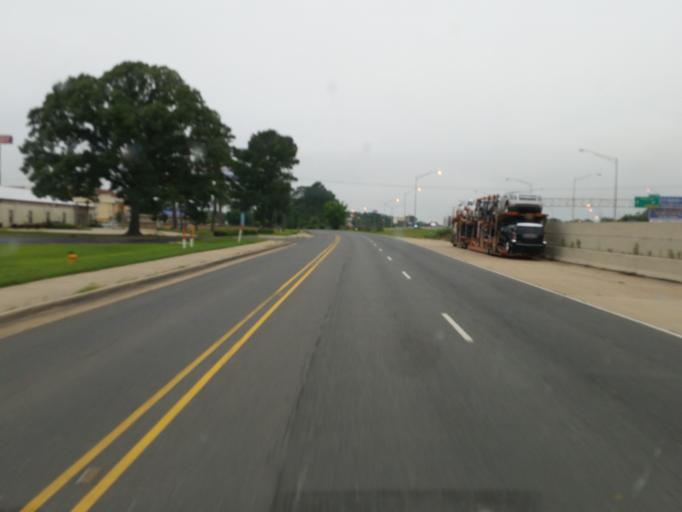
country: US
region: Louisiana
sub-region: Caddo Parish
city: Greenwood
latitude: 32.4512
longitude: -93.8593
